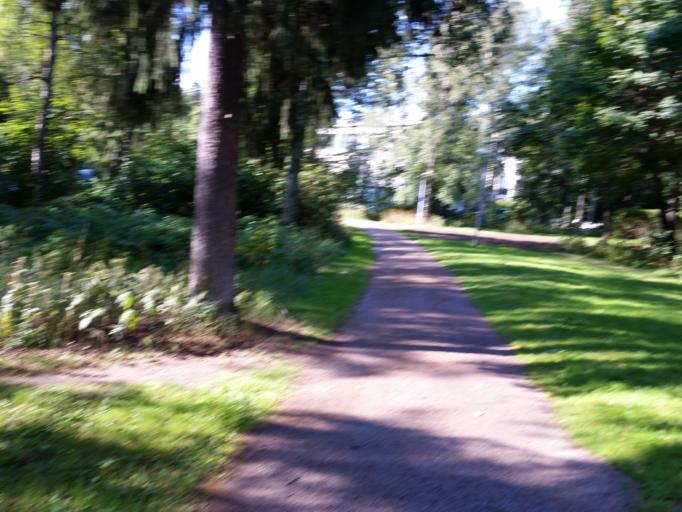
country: FI
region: Uusimaa
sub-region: Helsinki
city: Teekkarikylae
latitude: 60.2086
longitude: 24.8722
